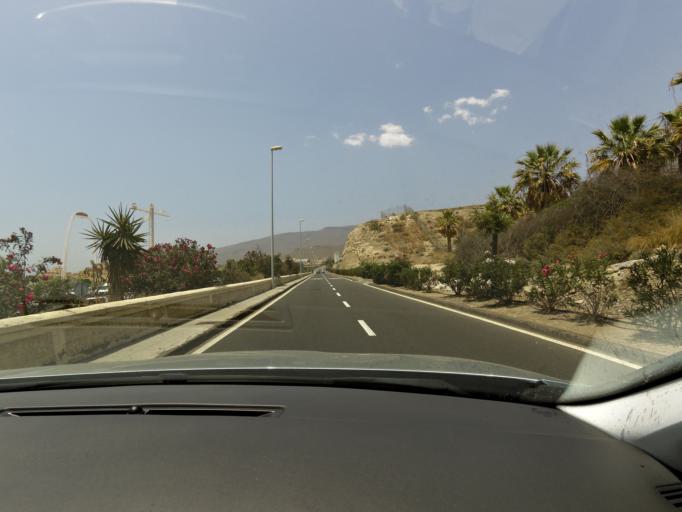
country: ES
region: Canary Islands
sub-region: Provincia de Santa Cruz de Tenerife
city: Playa de las Americas
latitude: 28.0830
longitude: -16.7290
